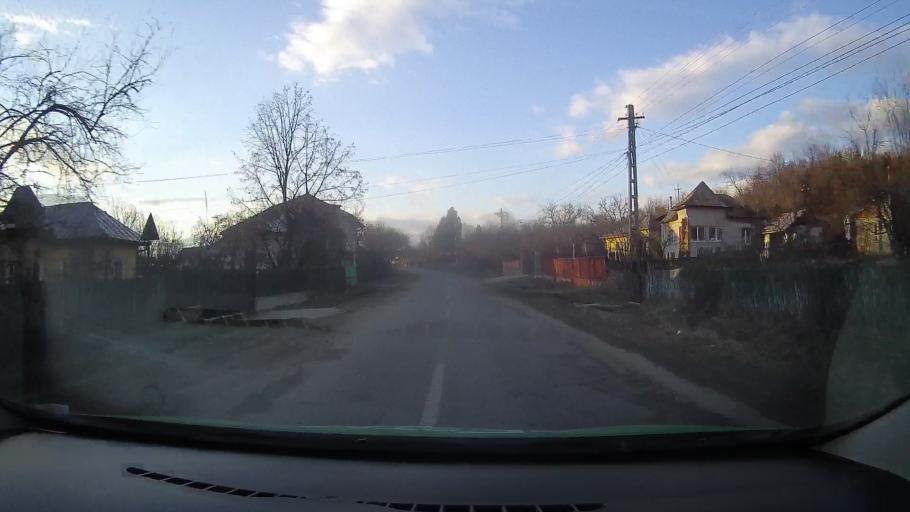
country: RO
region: Dambovita
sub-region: Comuna Gura Ocnitei
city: Adanca
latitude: 44.9193
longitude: 25.6161
